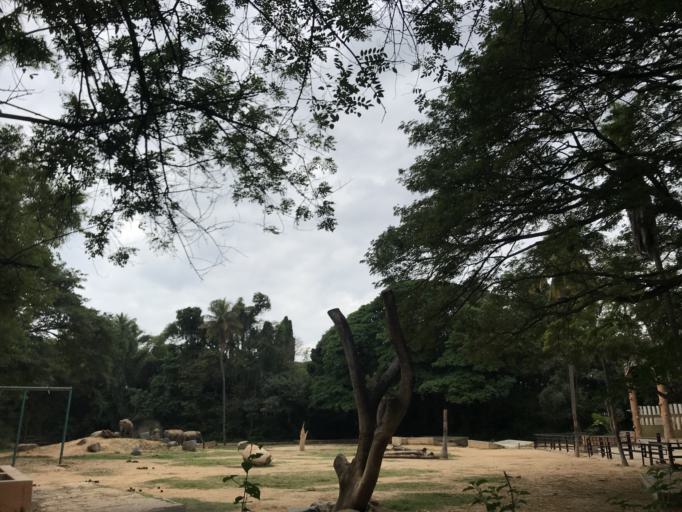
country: IN
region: Karnataka
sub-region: Mysore
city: Mysore
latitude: 12.3002
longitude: 76.6695
